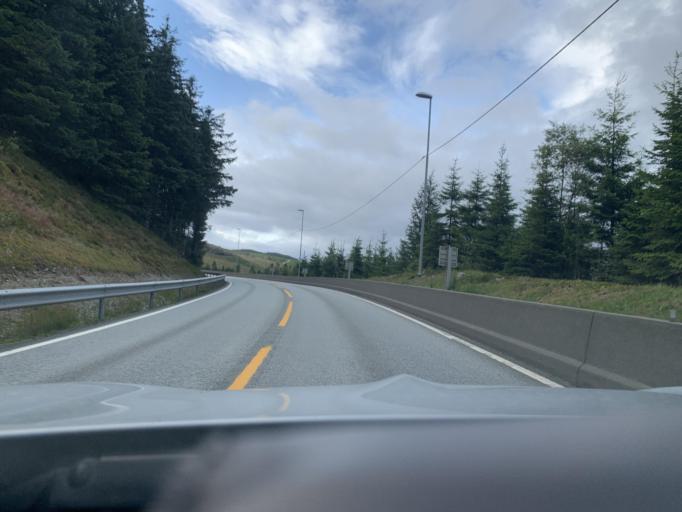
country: NO
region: Rogaland
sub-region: Bjerkreim
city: Vikesa
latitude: 58.6388
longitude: 6.0830
